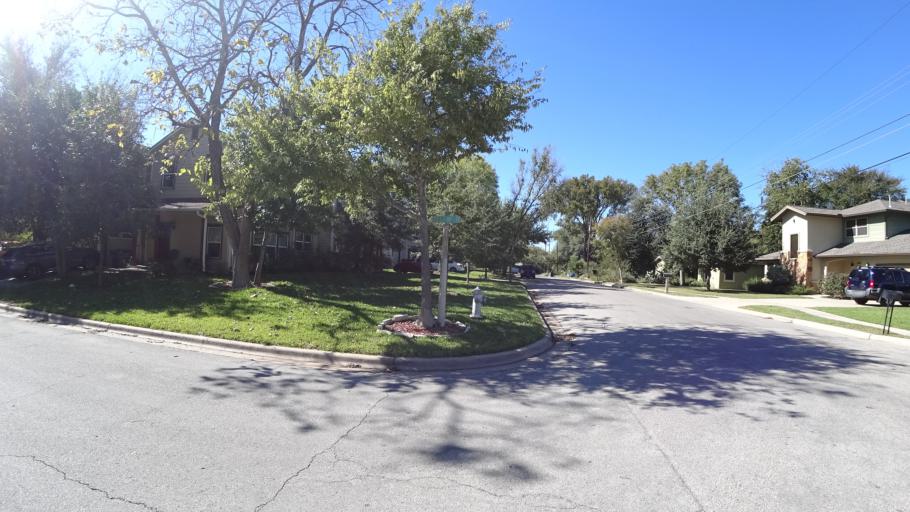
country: US
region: Texas
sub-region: Travis County
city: Rollingwood
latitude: 30.2260
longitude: -97.7790
